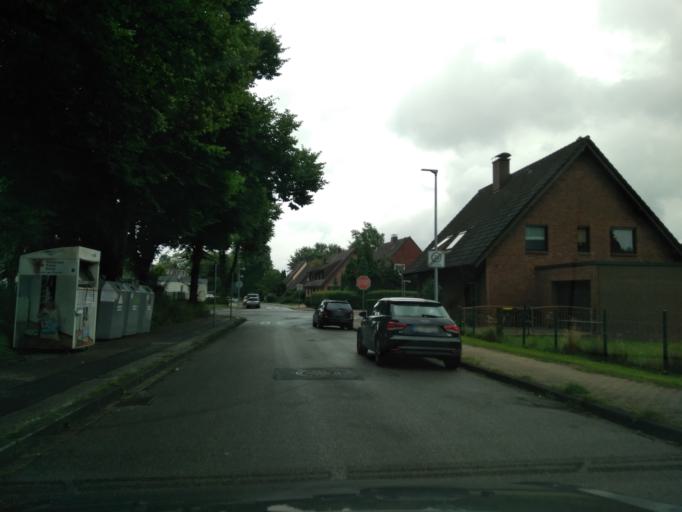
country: DE
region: North Rhine-Westphalia
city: Herten
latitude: 51.5777
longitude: 7.1036
